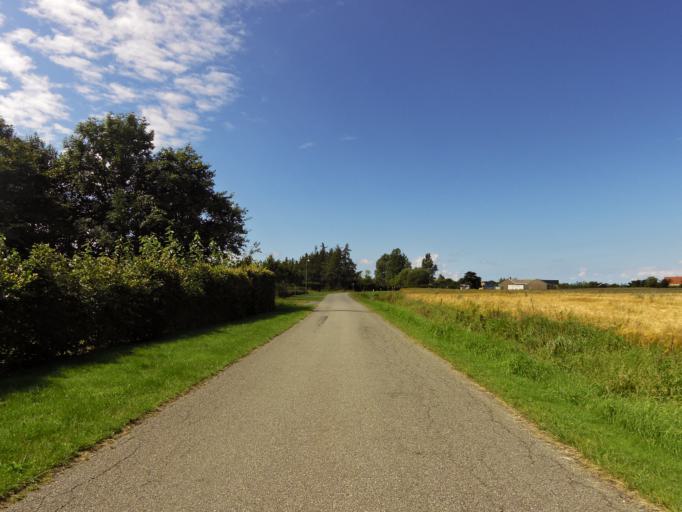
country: DK
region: South Denmark
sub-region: Esbjerg Kommune
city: Ribe
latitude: 55.3092
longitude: 8.7842
